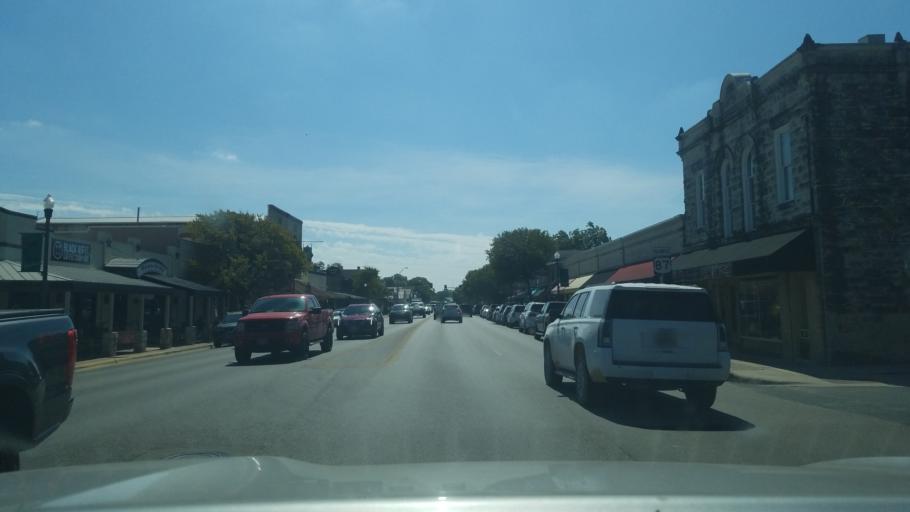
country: US
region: Texas
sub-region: Kendall County
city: Boerne
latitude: 29.7941
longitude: -98.7319
